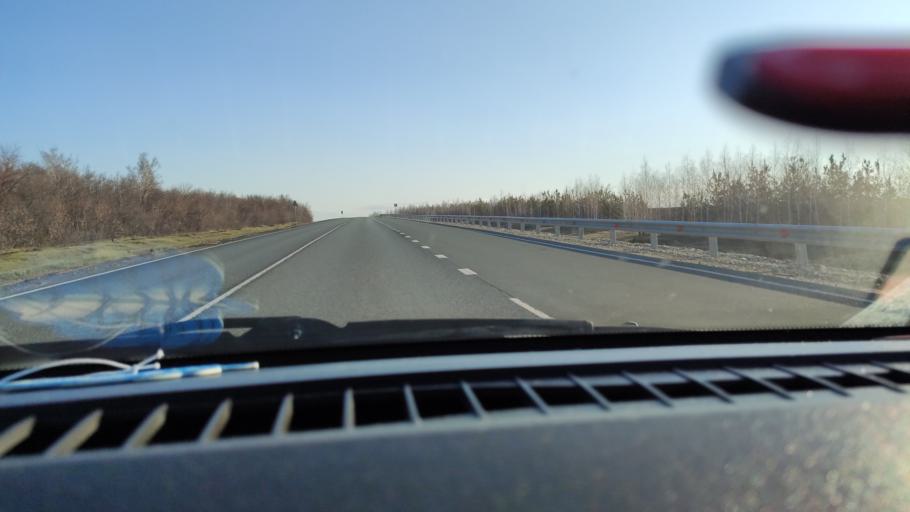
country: RU
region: Saratov
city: Balakovo
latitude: 52.1606
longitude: 47.8215
